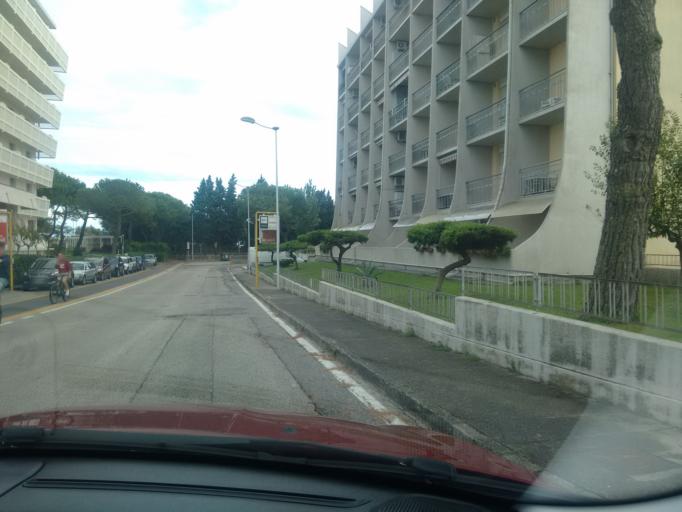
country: IT
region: Veneto
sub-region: Provincia di Venezia
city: Caorle
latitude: 45.5898
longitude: 12.8612
